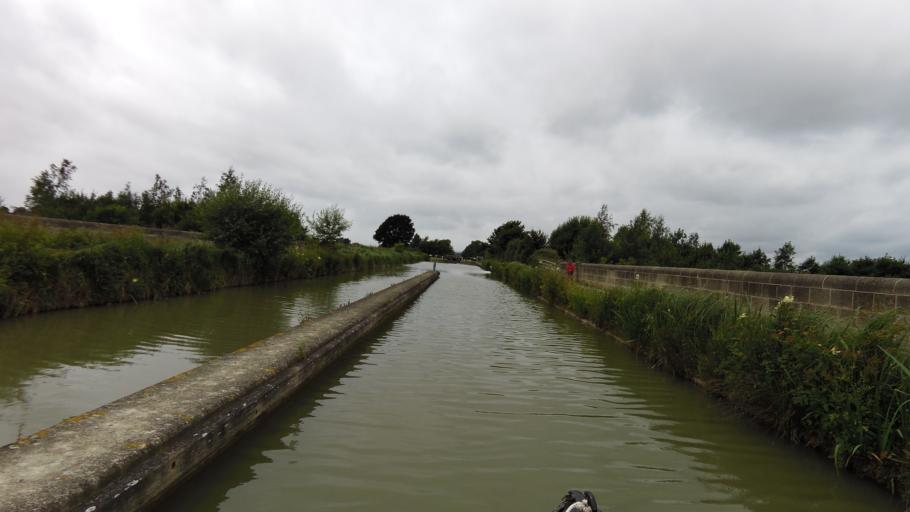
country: GB
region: England
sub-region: Wiltshire
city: Melksham
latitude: 51.3472
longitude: -2.1382
